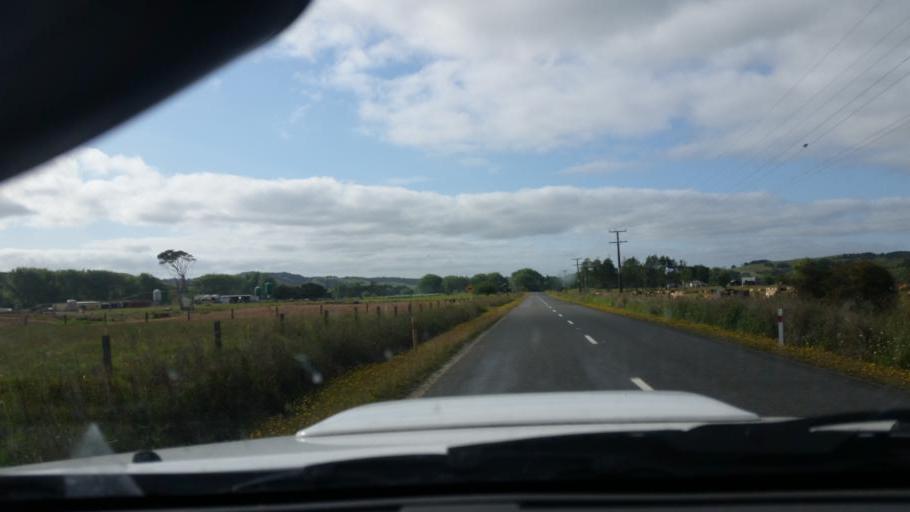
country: NZ
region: Northland
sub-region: Kaipara District
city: Dargaville
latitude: -35.8336
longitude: 173.8423
